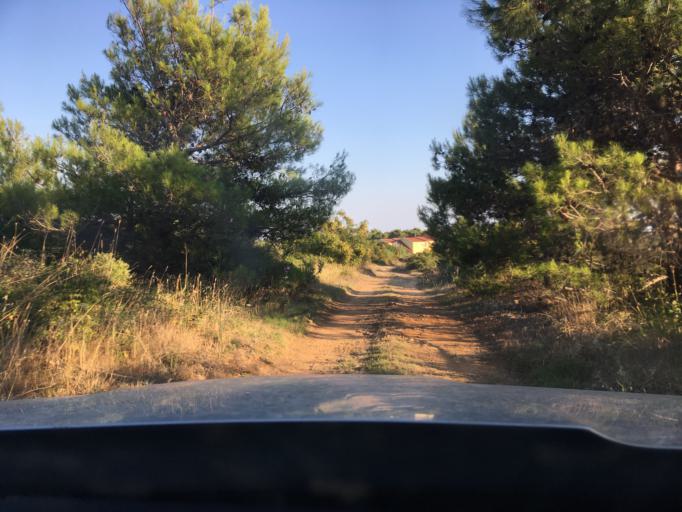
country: HR
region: Zadarska
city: Vir
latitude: 44.2978
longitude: 15.0751
